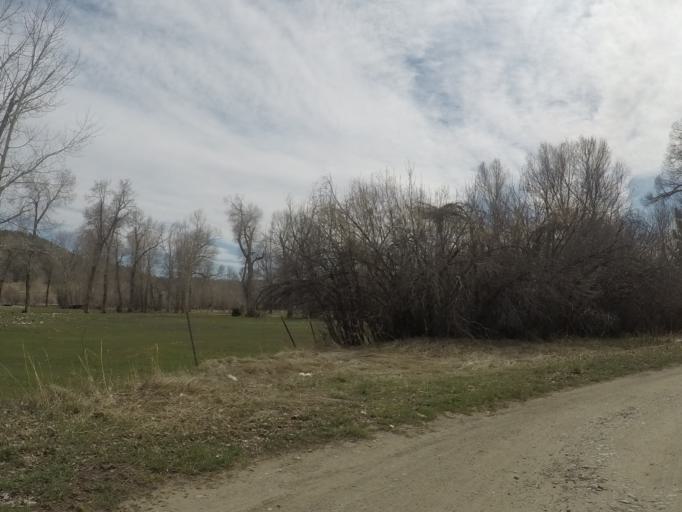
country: US
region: Montana
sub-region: Stillwater County
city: Columbus
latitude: 45.5841
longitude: -109.3315
